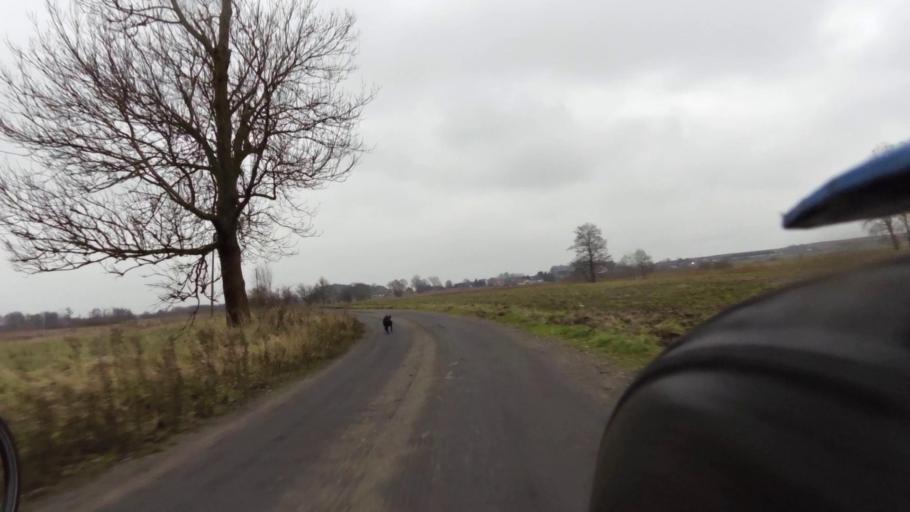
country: PL
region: West Pomeranian Voivodeship
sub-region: Powiat szczecinecki
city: Szczecinek
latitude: 53.6658
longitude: 16.6618
